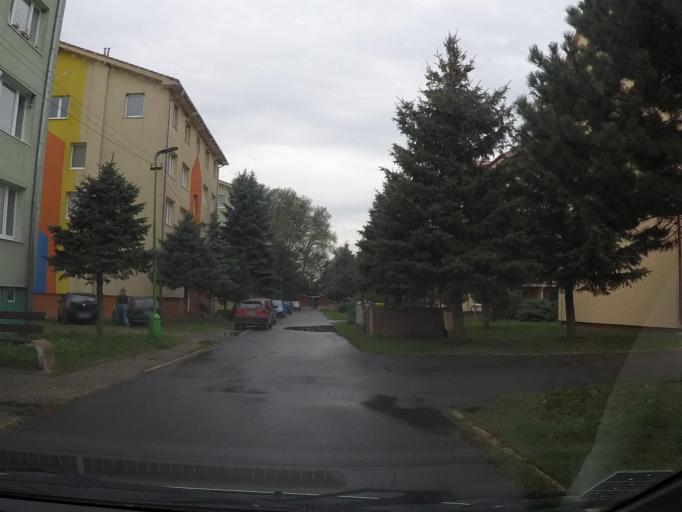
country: SK
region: Banskobystricky
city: Dudince
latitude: 48.1886
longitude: 18.8485
